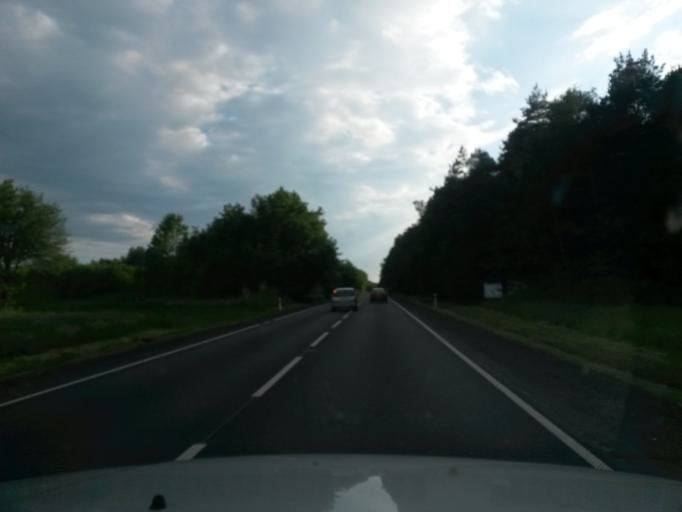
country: PL
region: Lodz Voivodeship
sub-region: Powiat belchatowski
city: Druzbice
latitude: 51.4043
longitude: 19.4435
